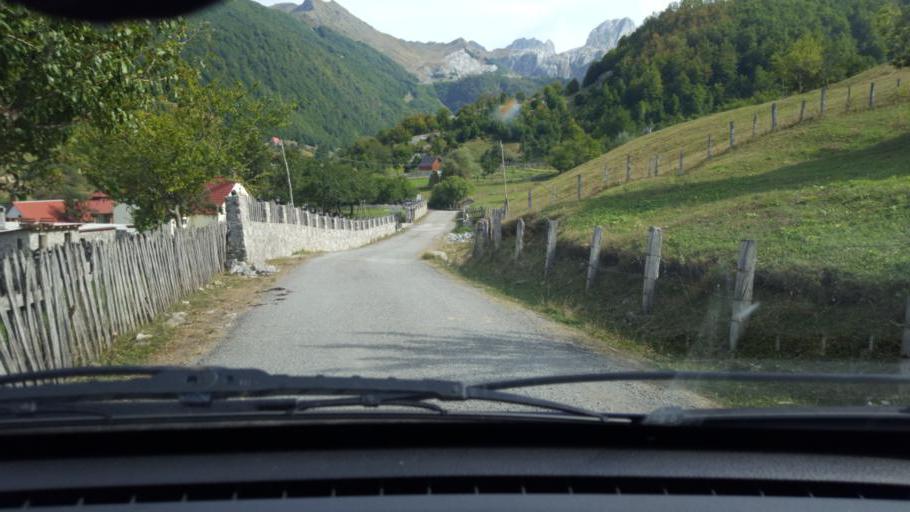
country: AL
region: Kukes
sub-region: Rrethi i Tropojes
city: Valbone
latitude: 42.5293
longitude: 19.7256
